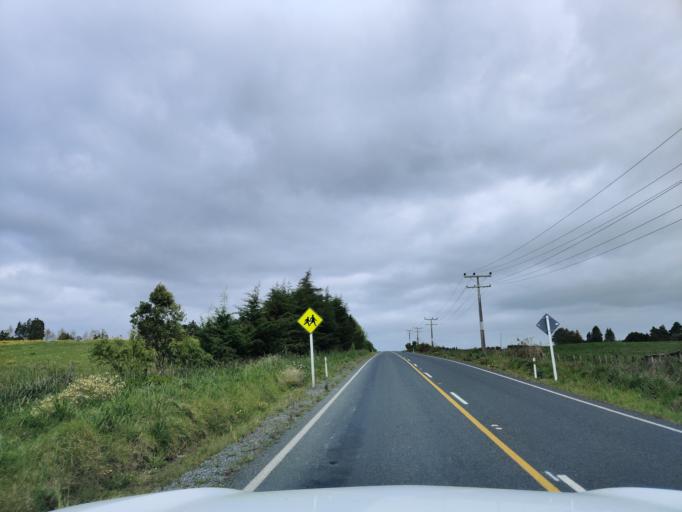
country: NZ
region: Waikato
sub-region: Waikato District
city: Ngaruawahia
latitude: -37.5776
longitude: 175.1371
